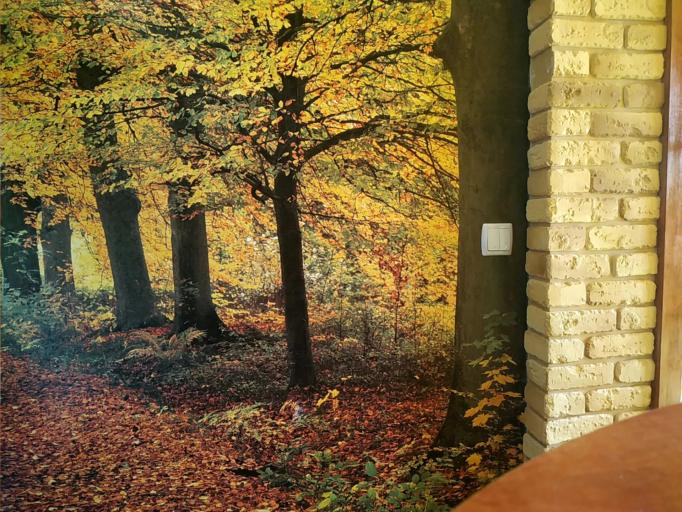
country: RU
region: Jaroslavl
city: Kukoboy
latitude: 58.9010
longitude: 39.6933
